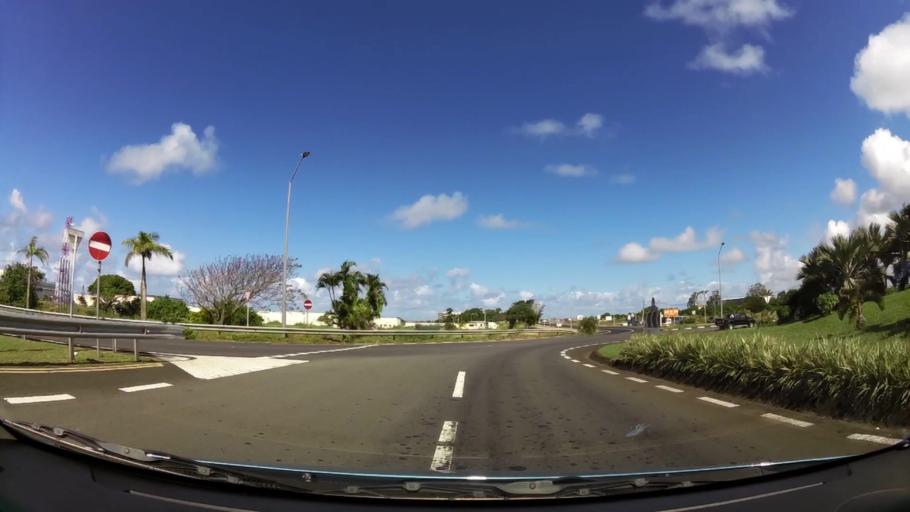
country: MU
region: Grand Port
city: Plaine Magnien
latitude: -20.4346
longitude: 57.6744
